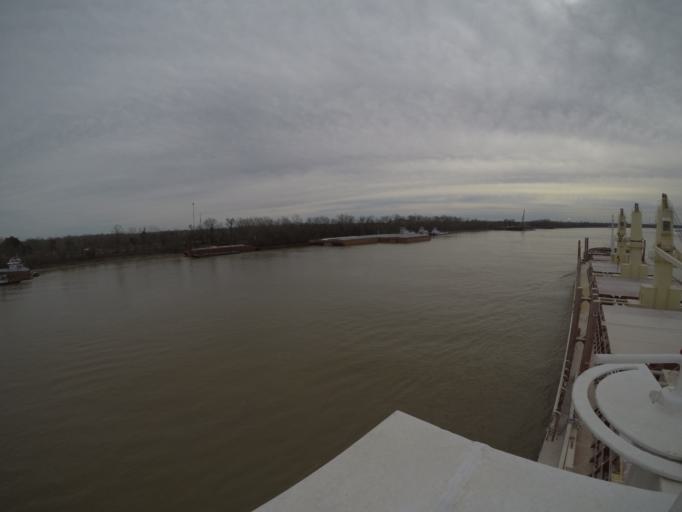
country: US
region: Louisiana
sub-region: Saint John the Baptist Parish
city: Laplace
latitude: 30.0448
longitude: -90.4758
